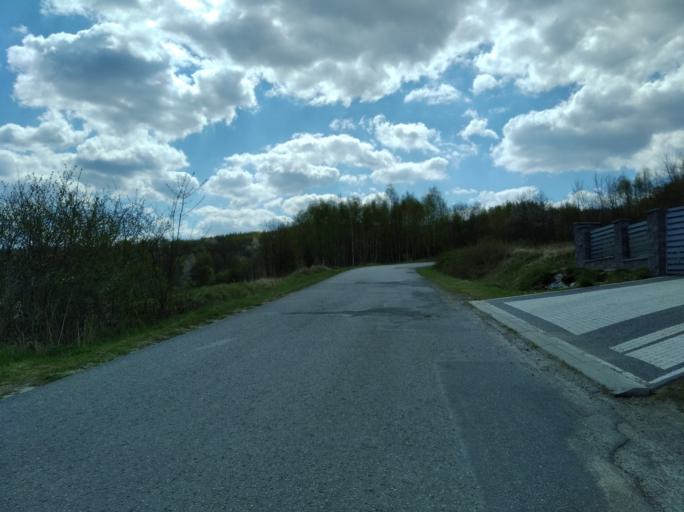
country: PL
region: Subcarpathian Voivodeship
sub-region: Powiat brzozowski
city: Wesola
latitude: 49.7724
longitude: 22.1331
